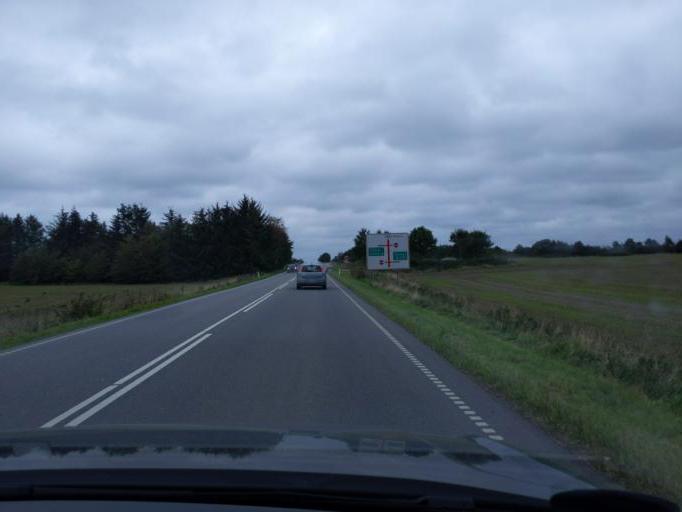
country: DK
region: North Denmark
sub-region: Mariagerfjord Kommune
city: Hobro
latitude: 56.5775
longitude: 9.8137
